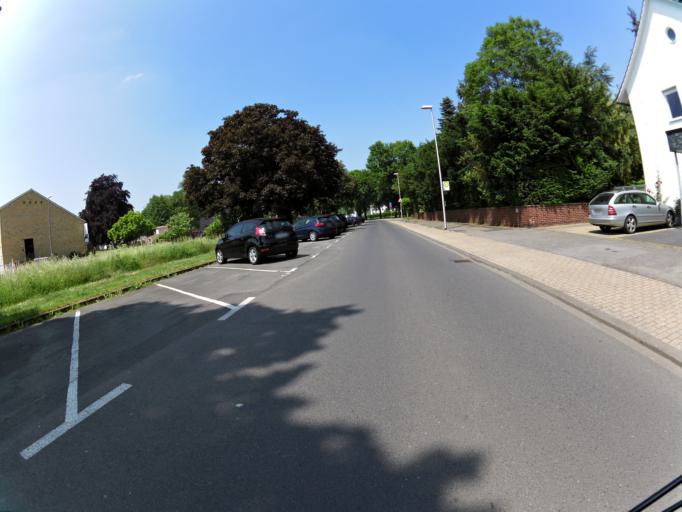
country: DE
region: North Rhine-Westphalia
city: Julich
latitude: 50.9176
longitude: 6.3611
